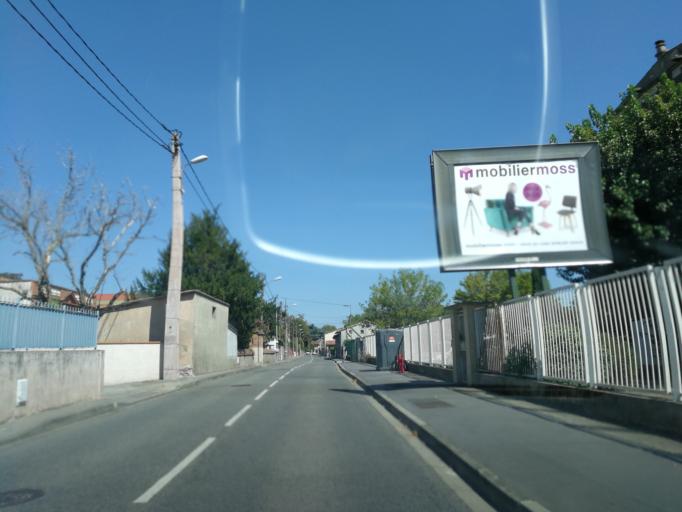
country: FR
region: Midi-Pyrenees
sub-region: Departement de la Haute-Garonne
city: Toulouse
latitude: 43.6338
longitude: 1.4587
